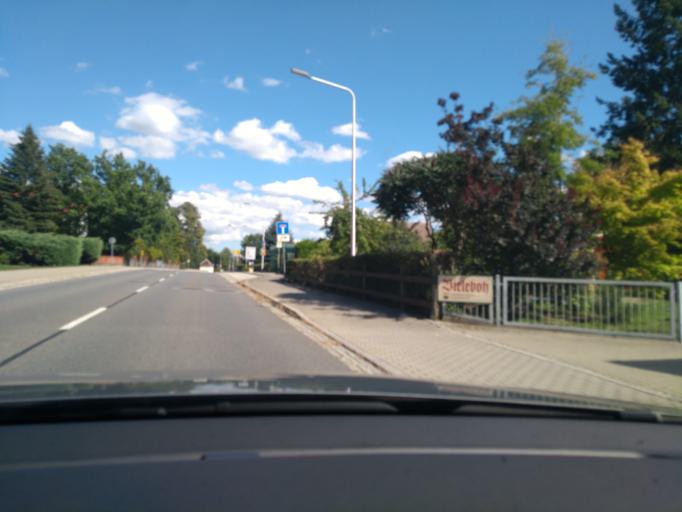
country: DE
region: Saxony
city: Goda
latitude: 51.1791
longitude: 14.3189
